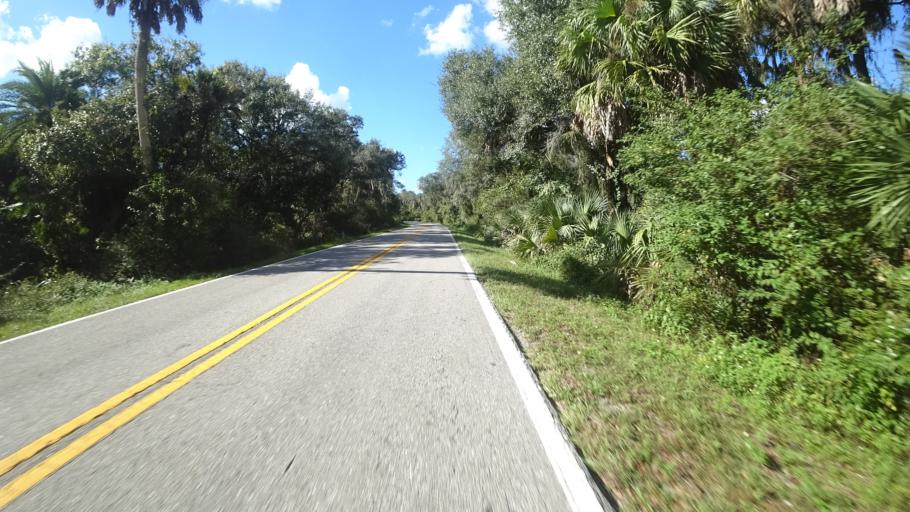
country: US
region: Florida
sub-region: Sarasota County
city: Lake Sarasota
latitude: 27.3045
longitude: -82.2584
